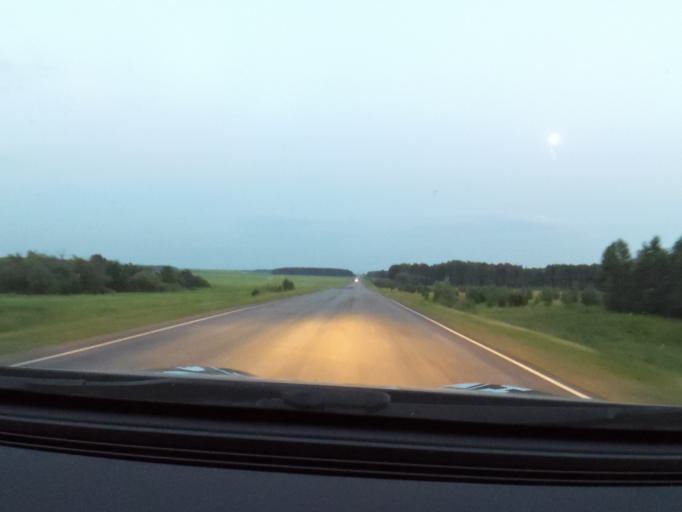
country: RU
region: Bashkortostan
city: Duvan
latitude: 56.1016
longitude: 58.0630
